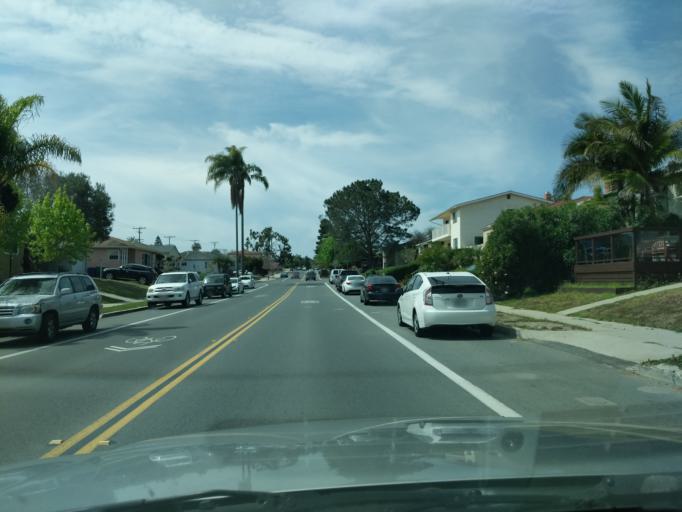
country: US
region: California
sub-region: San Diego County
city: Coronado
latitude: 32.7349
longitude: -117.2403
